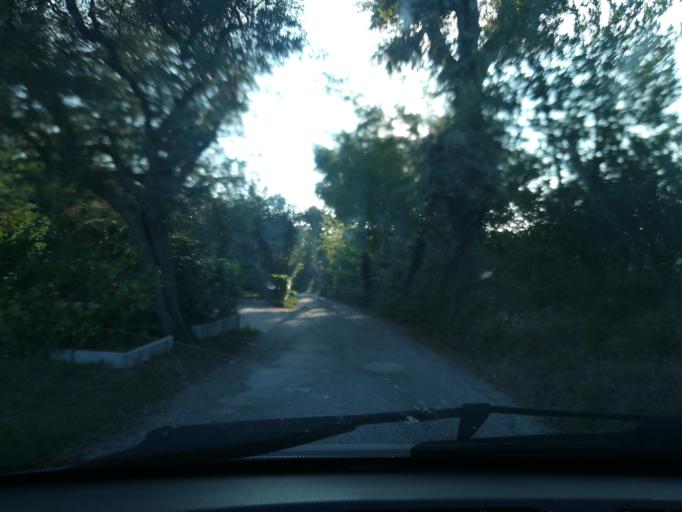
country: IT
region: The Marches
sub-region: Provincia di Macerata
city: Macerata
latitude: 43.2861
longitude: 13.4592
